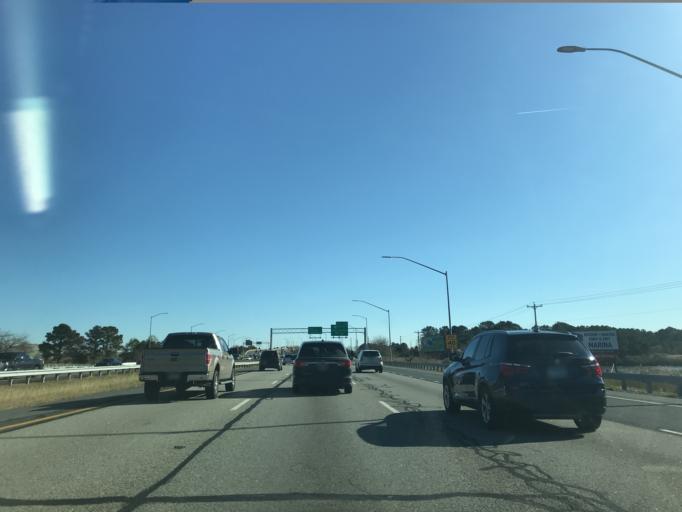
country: US
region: Maryland
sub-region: Queen Anne's County
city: Chester
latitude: 38.9727
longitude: -76.2603
